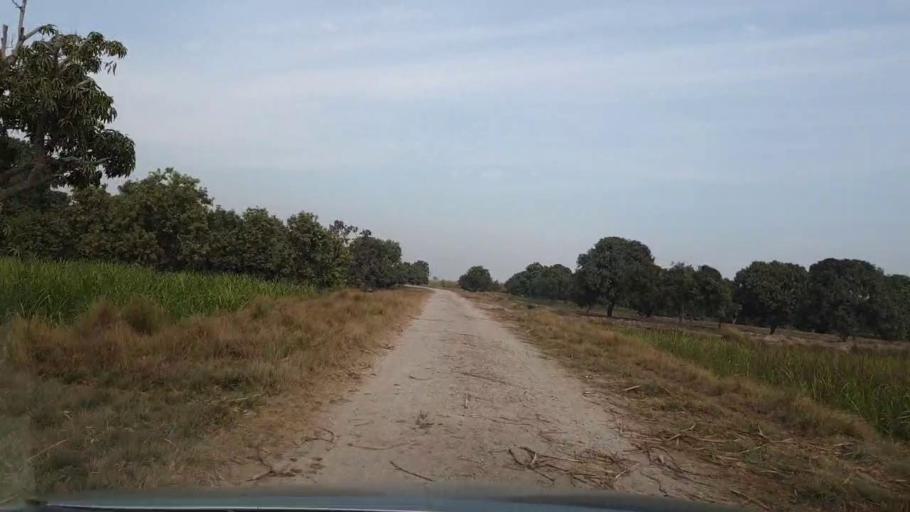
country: PK
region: Sindh
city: Matiari
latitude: 25.5613
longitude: 68.5410
